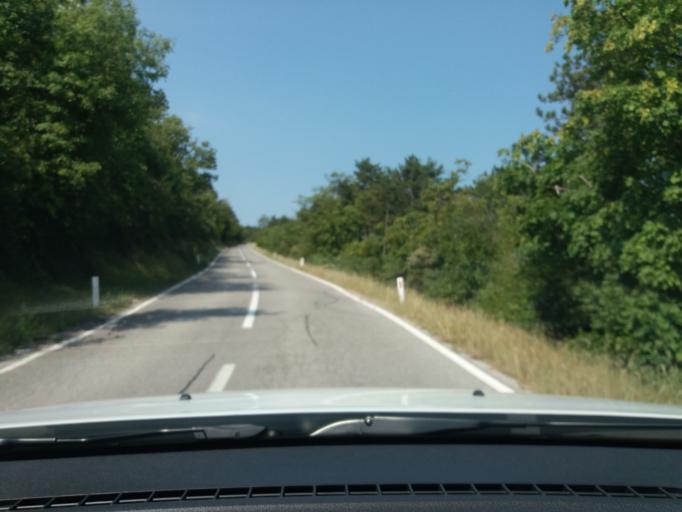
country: SI
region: Miren-Kostanjevica
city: Miren
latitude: 45.8790
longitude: 13.6007
